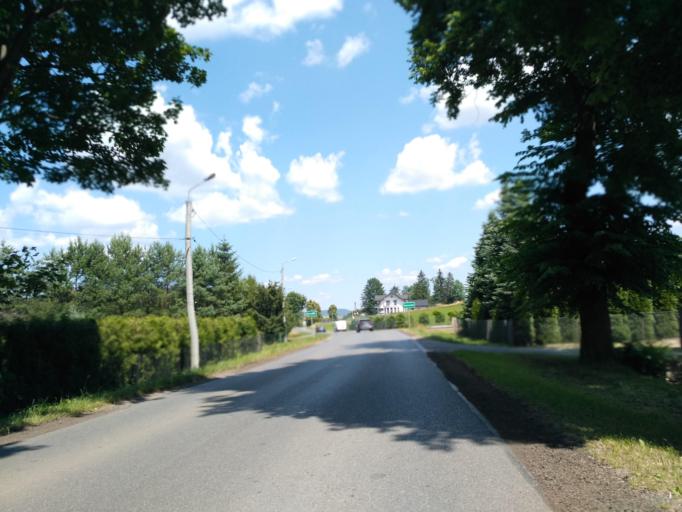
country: PL
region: Subcarpathian Voivodeship
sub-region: Powiat sanocki
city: Niebieszczany
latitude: 49.5414
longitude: 22.1327
